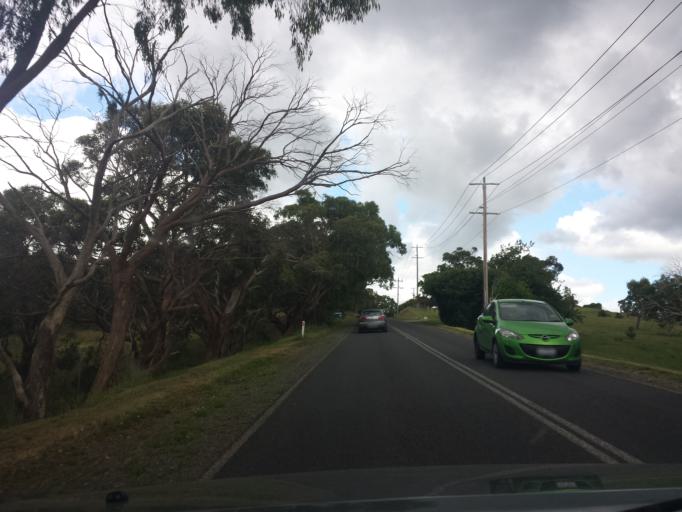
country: AU
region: Victoria
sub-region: Yarra Ranges
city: Tremont
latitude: -37.9098
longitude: 145.3105
